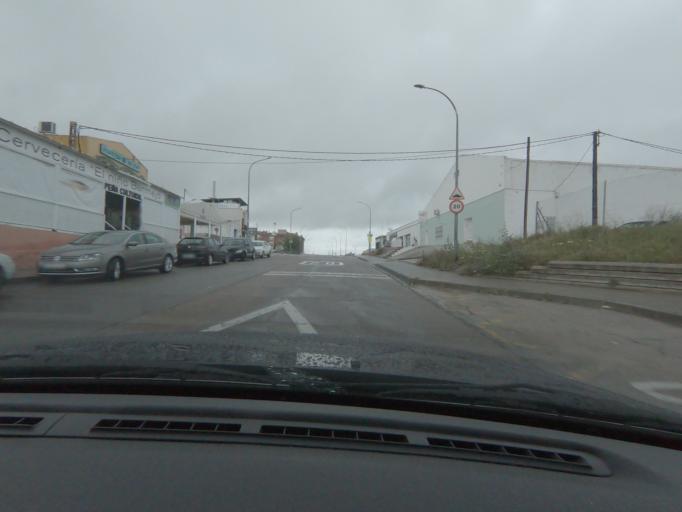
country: ES
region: Extremadura
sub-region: Provincia de Badajoz
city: Merida
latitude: 38.9268
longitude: -6.3377
